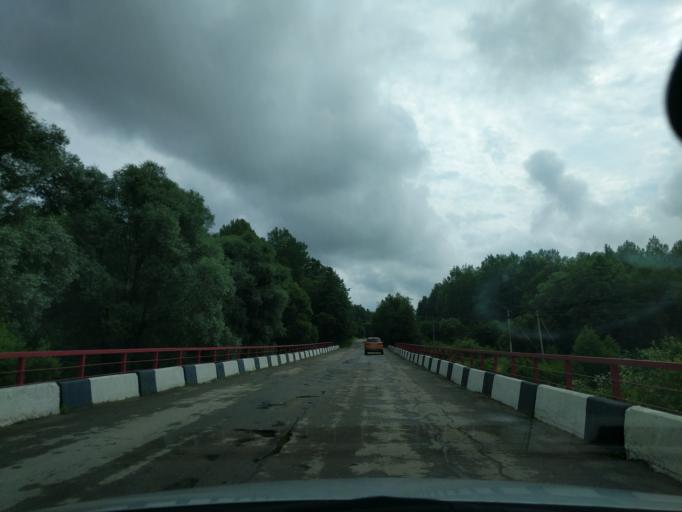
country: RU
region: Kaluga
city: Nikola-Lenivets
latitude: 54.7652
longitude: 35.7073
